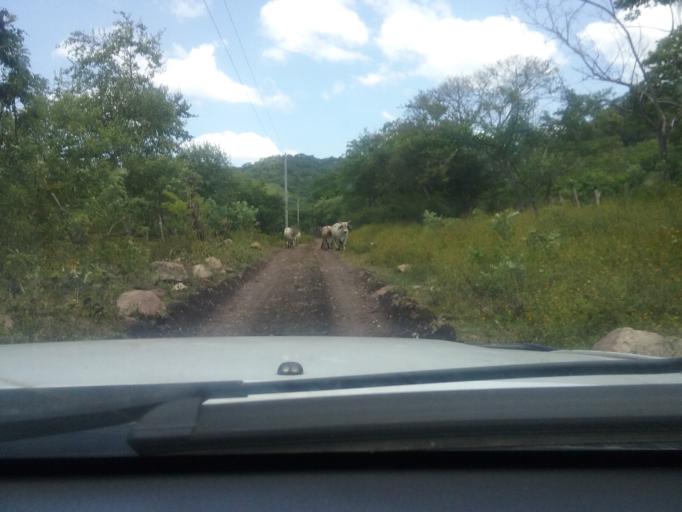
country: NI
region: Matagalpa
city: Terrabona
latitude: 12.6539
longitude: -86.0046
